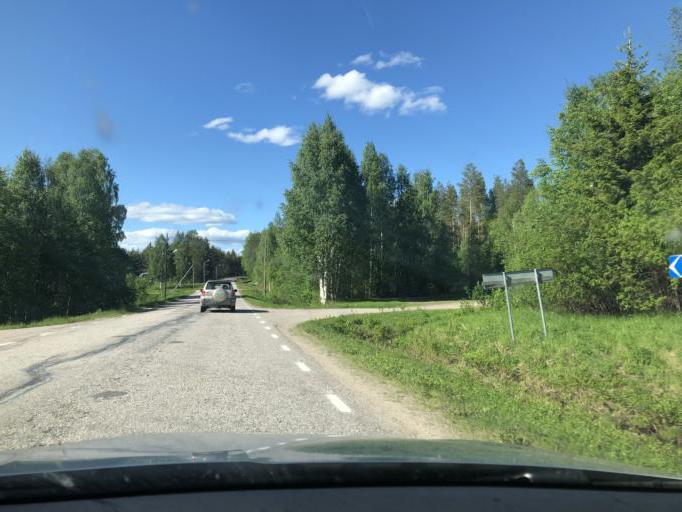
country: SE
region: Norrbotten
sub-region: Kalix Kommun
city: Kalix
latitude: 66.0093
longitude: 23.1431
